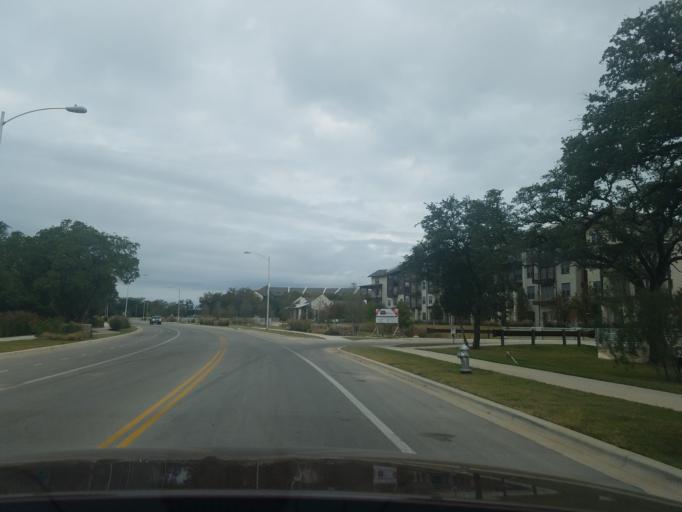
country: US
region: Texas
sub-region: Williamson County
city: Anderson Mill
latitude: 30.4741
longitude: -97.7843
